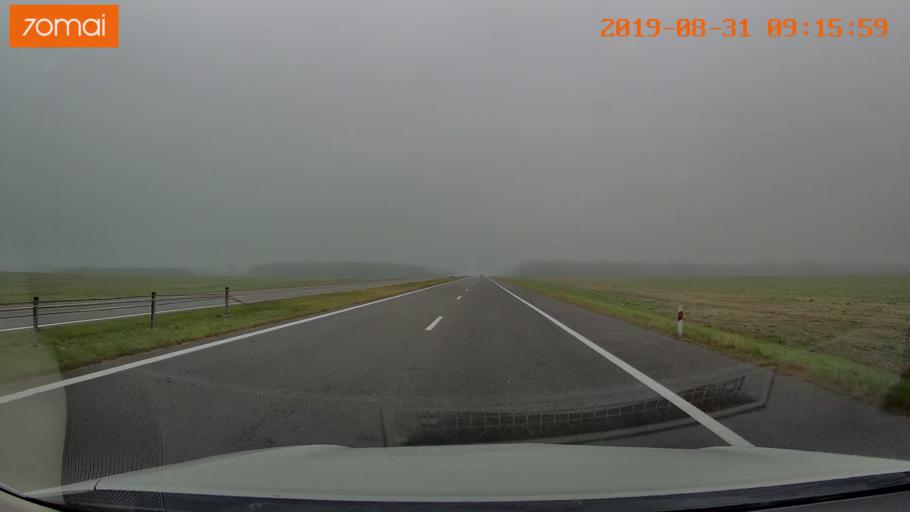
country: BY
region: Minsk
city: Chervyen'
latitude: 53.7685
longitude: 28.6961
